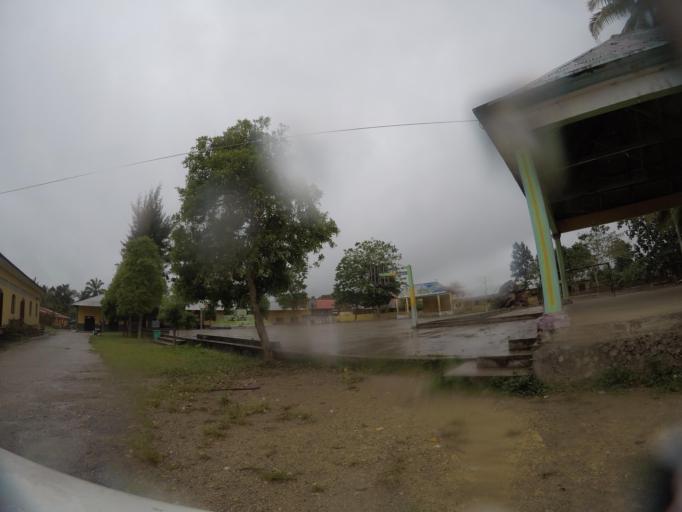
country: TL
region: Lautem
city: Lospalos
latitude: -8.5222
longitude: 126.9966
